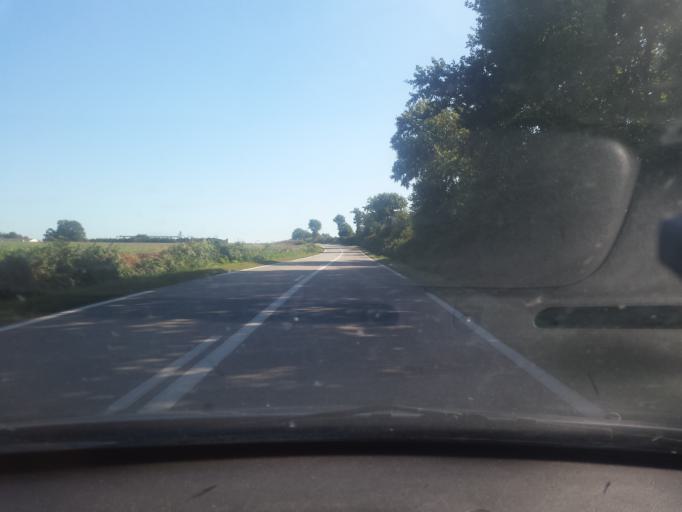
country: FR
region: Brittany
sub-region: Departement du Morbihan
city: Saint-Thuriau
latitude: 48.0328
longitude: -2.9199
